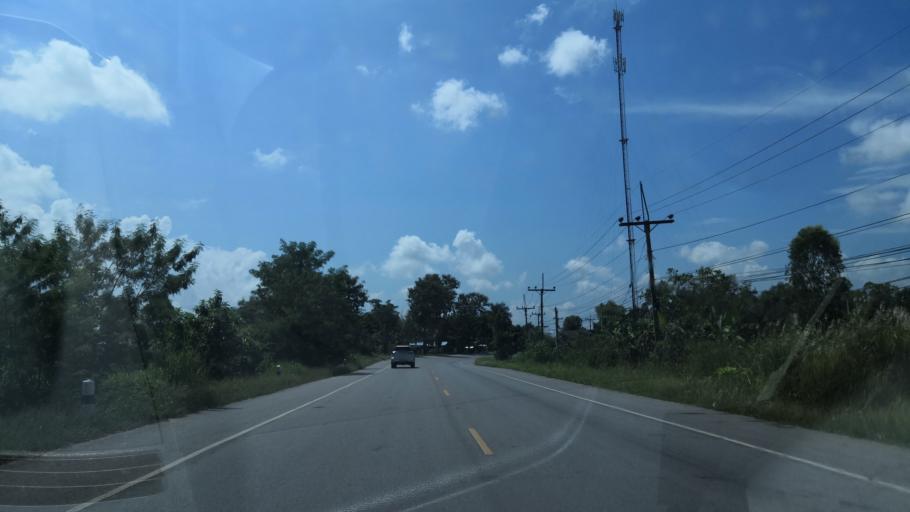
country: TH
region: Chiang Rai
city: Wiang Chiang Rung
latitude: 19.9666
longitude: 100.0109
